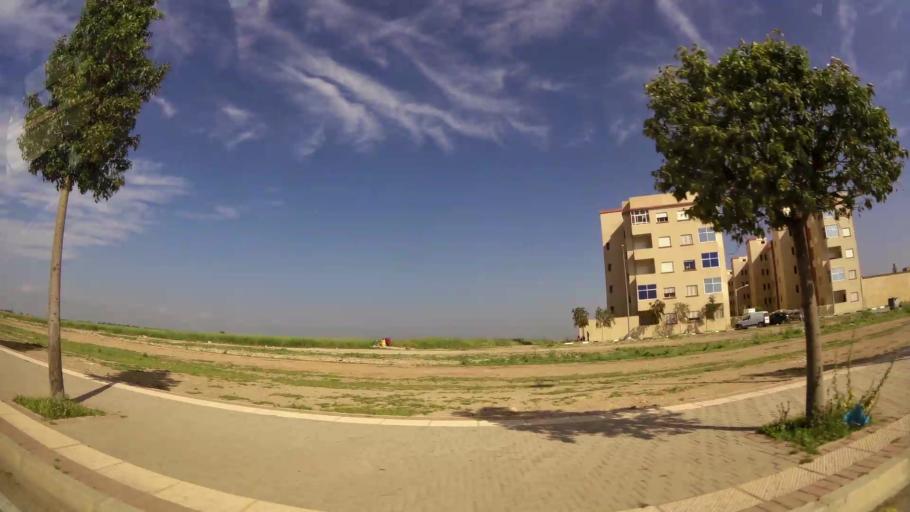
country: MA
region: Oriental
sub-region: Oujda-Angad
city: Oujda
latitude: 34.7161
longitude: -1.8837
